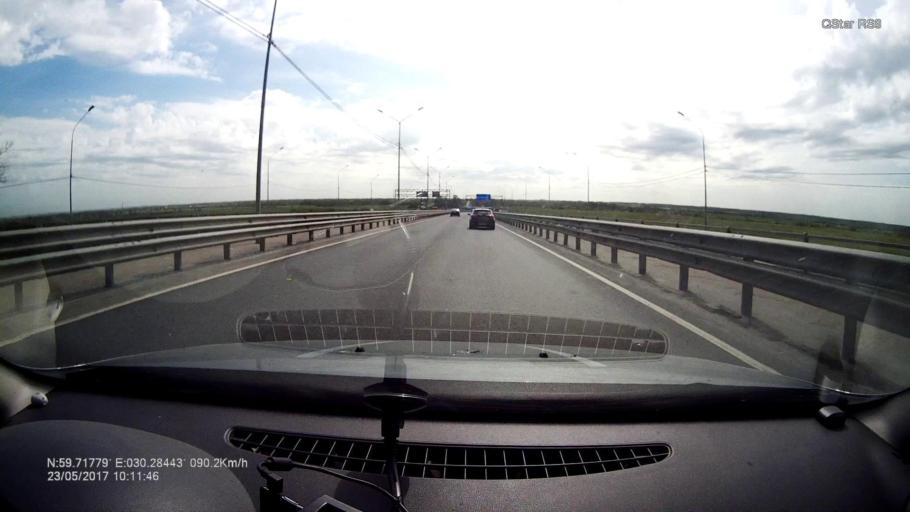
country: RU
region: St.-Petersburg
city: Aleksandrovskaya
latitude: 59.7176
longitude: 30.2851
